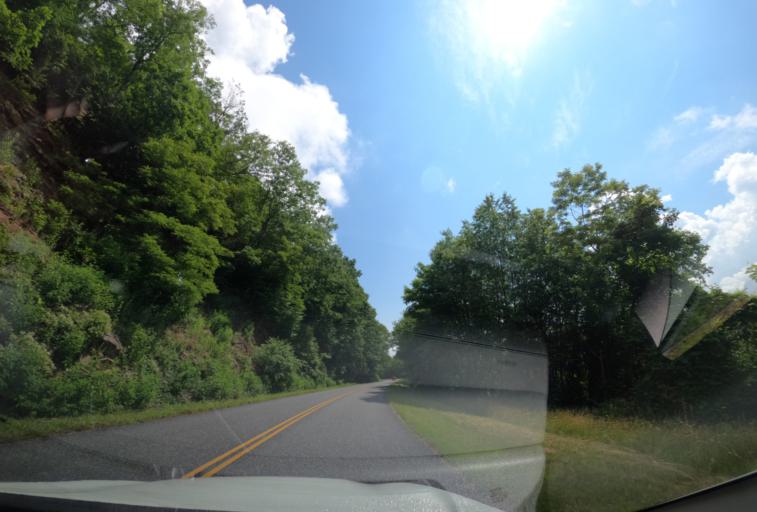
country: US
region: North Carolina
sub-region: Haywood County
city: Hazelwood
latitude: 35.4320
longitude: -83.0353
